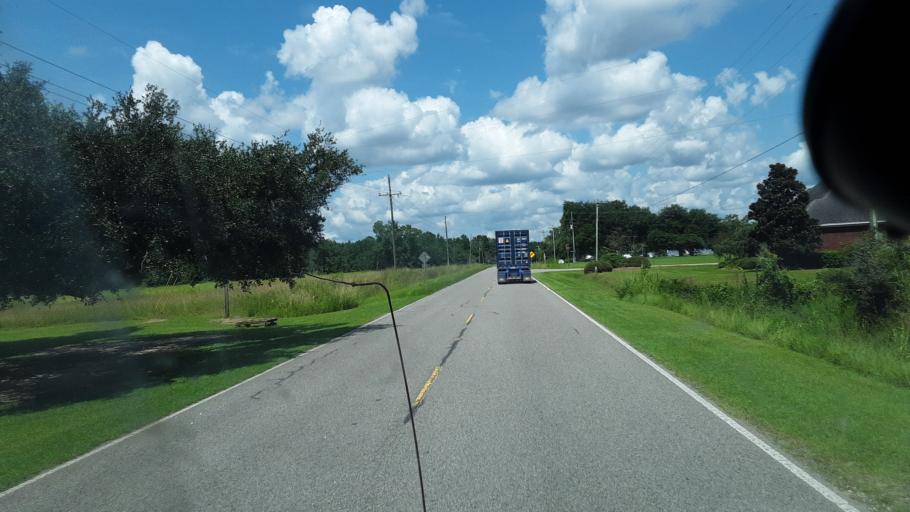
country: US
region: South Carolina
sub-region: Williamsburg County
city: Andrews
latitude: 33.4377
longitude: -79.5921
